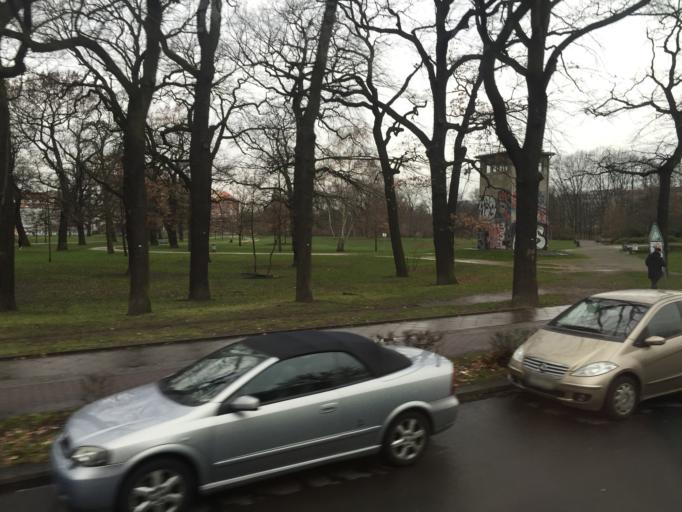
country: DE
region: Berlin
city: Berlin Treptow
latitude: 52.4957
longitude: 13.4515
